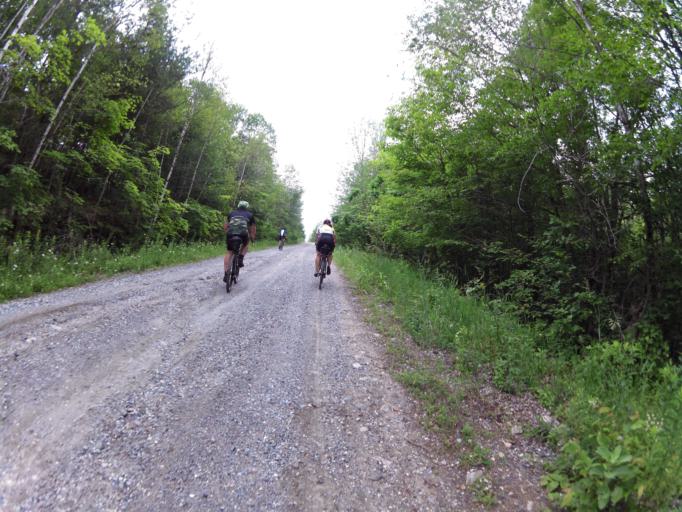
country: CA
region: Ontario
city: Perth
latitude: 45.0262
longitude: -76.5718
